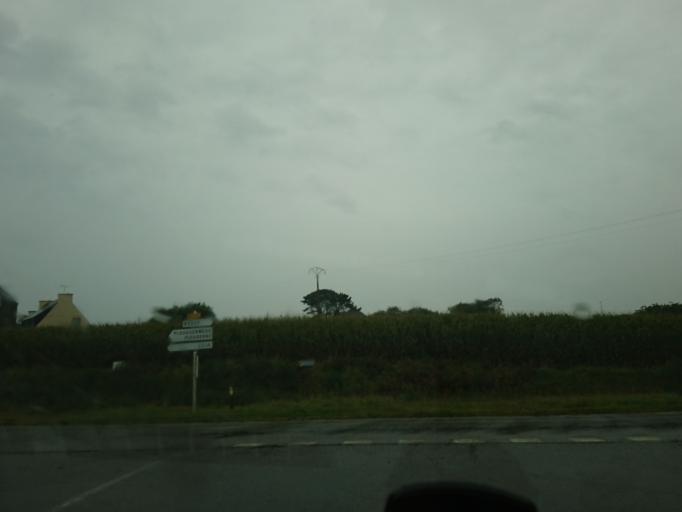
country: FR
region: Brittany
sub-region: Departement du Finistere
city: Plouguerneau
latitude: 48.6003
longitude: -4.5122
